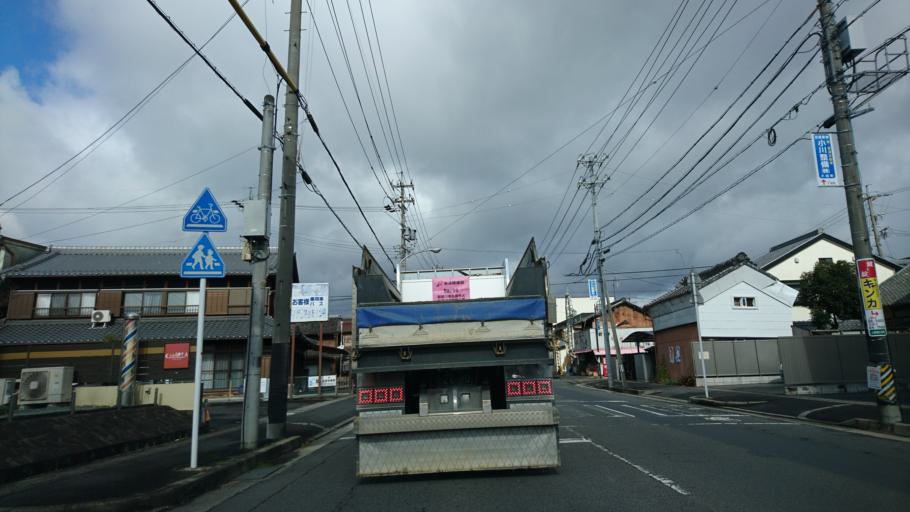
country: JP
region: Mie
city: Ueno-ebisumachi
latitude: 34.7660
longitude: 136.1232
